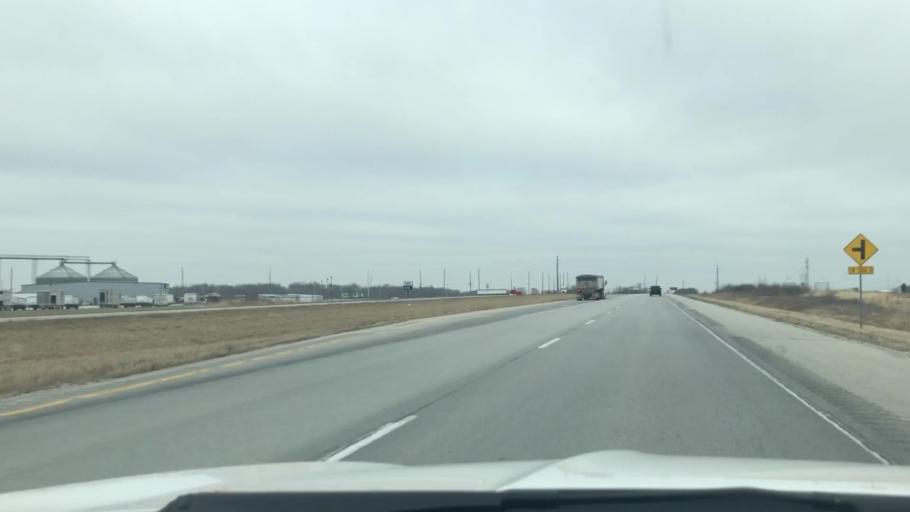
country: US
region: Indiana
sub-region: Cass County
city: Dunkirk
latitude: 40.7178
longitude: -86.4290
